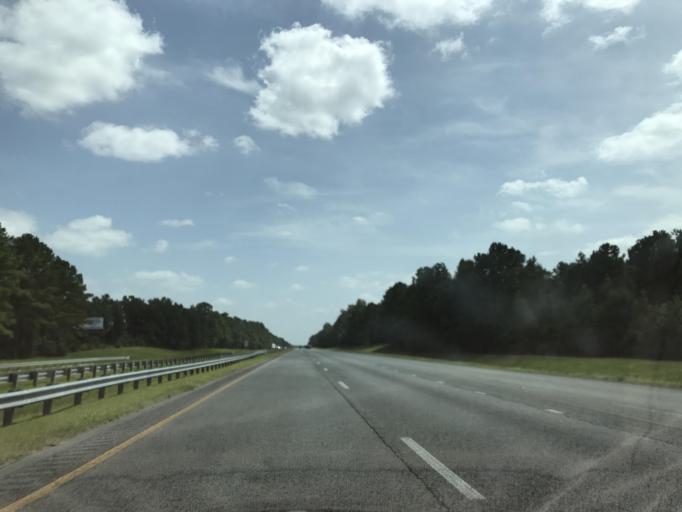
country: US
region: North Carolina
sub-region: Duplin County
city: Kenansville
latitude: 34.9146
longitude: -78.0218
